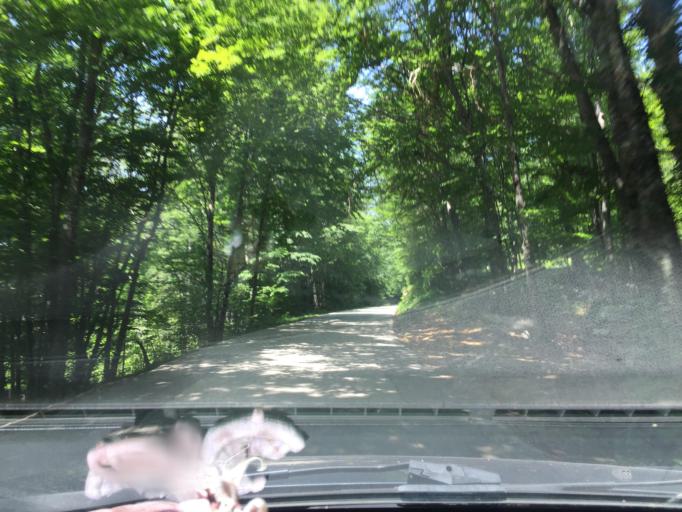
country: HR
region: Istarska
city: Buzet
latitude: 45.4696
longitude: 14.1112
